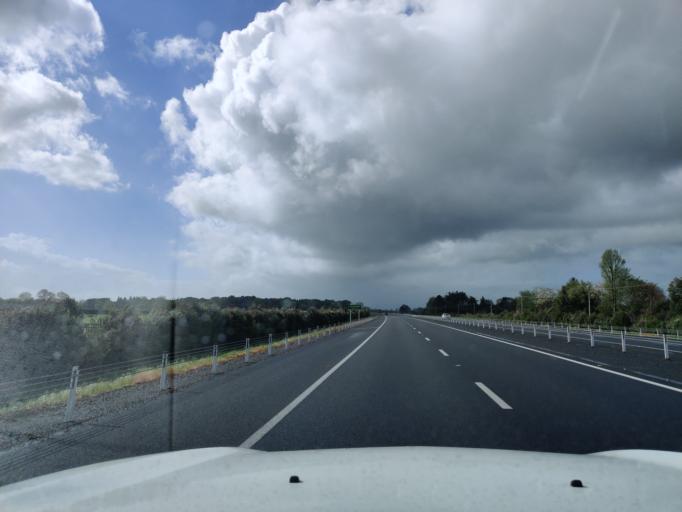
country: NZ
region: Waikato
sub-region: Waipa District
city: Cambridge
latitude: -37.8576
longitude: 175.3956
